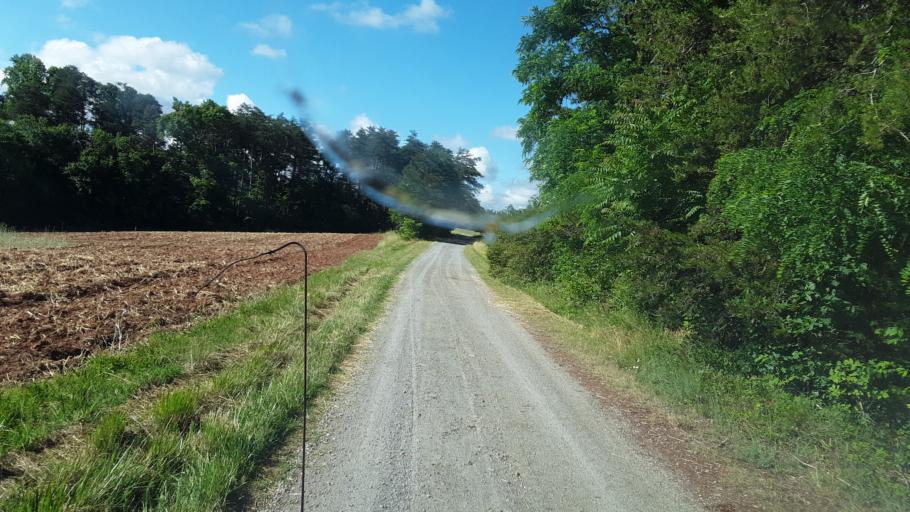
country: US
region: Virginia
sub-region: Pittsylvania County
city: Chatham
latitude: 36.8390
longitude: -79.4173
